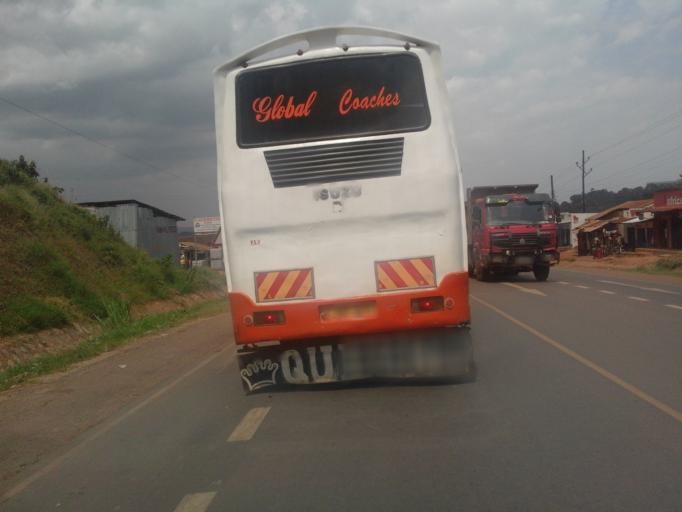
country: UG
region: Central Region
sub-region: Mpigi District
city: Mpigi
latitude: 0.2440
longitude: 32.3790
